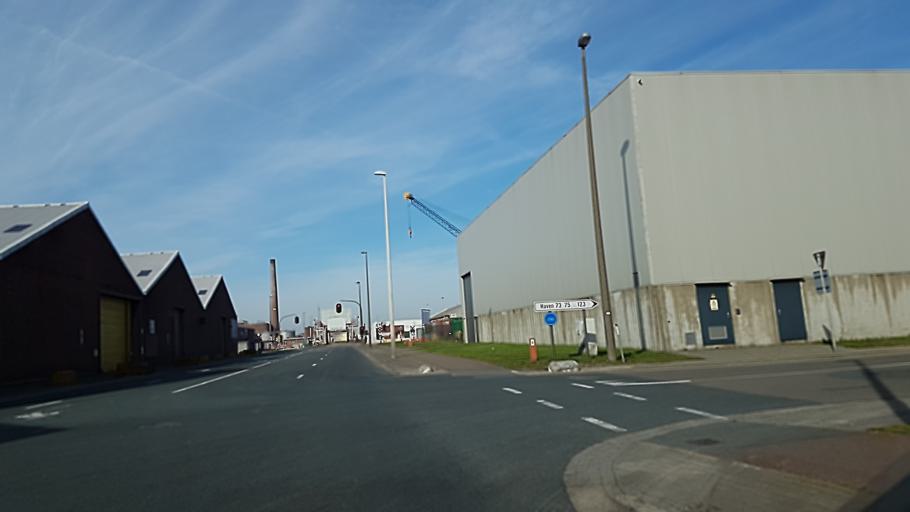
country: BE
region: Flanders
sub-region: Provincie Antwerpen
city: Antwerpen
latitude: 51.2576
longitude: 4.3887
